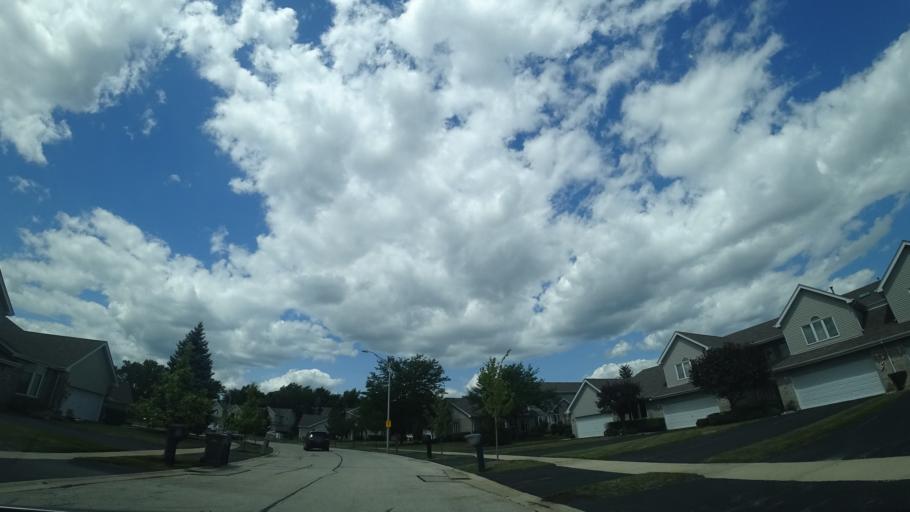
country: US
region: Illinois
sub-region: Will County
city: Homer Glen
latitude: 41.5841
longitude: -87.8959
